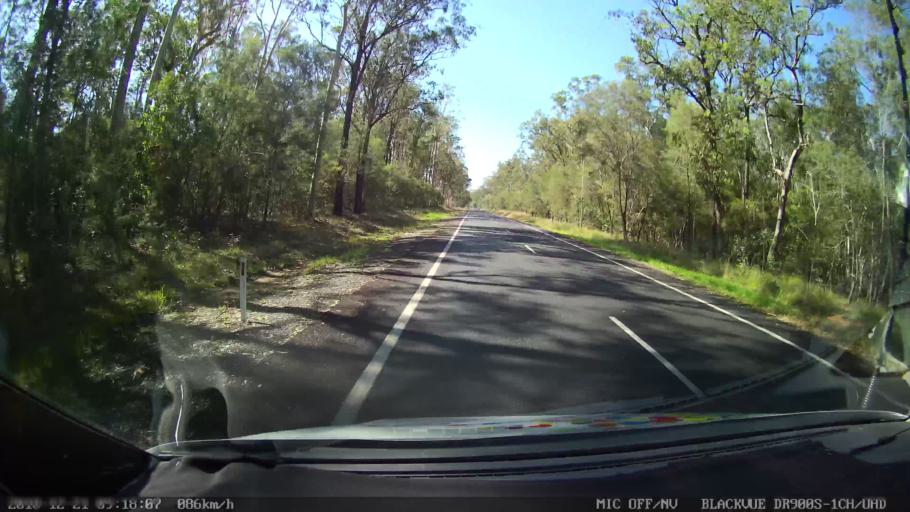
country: AU
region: New South Wales
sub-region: Clarence Valley
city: Maclean
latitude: -29.3003
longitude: 152.9930
